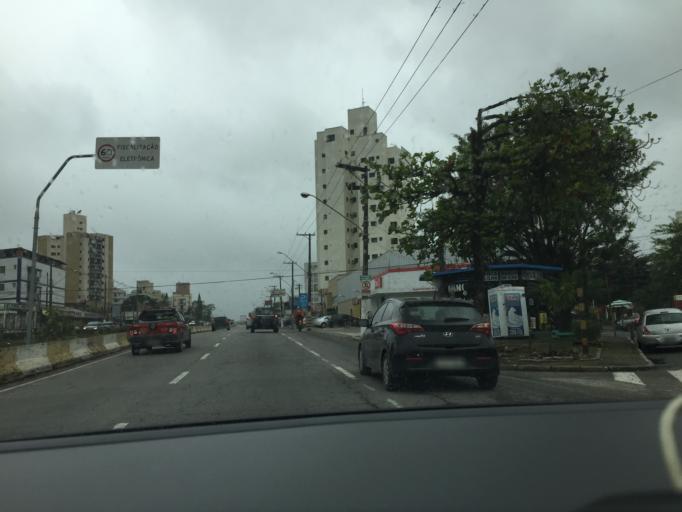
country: BR
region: Sao Paulo
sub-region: Guaruja
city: Guaruja
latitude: -23.9813
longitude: -46.2272
